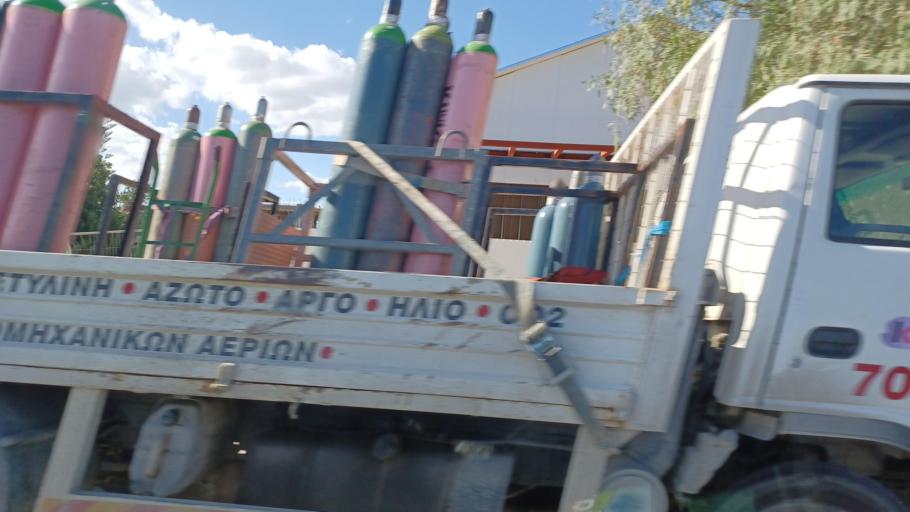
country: CY
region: Limassol
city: Pyrgos
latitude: 34.7320
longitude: 33.2048
